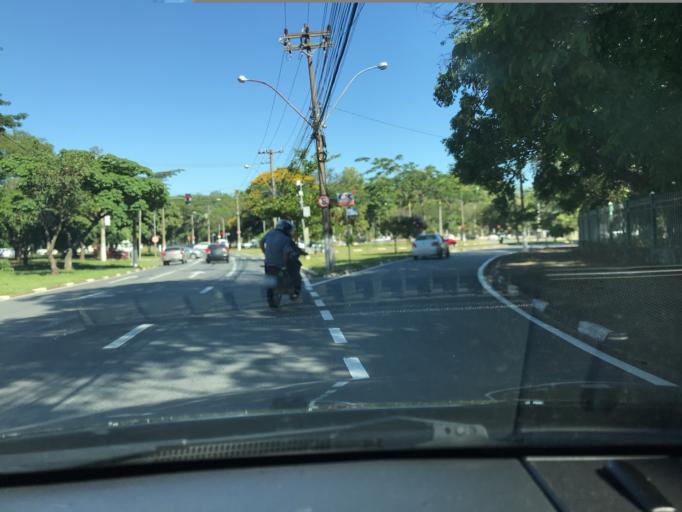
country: BR
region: Sao Paulo
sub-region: Campinas
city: Campinas
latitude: -22.8771
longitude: -47.0759
